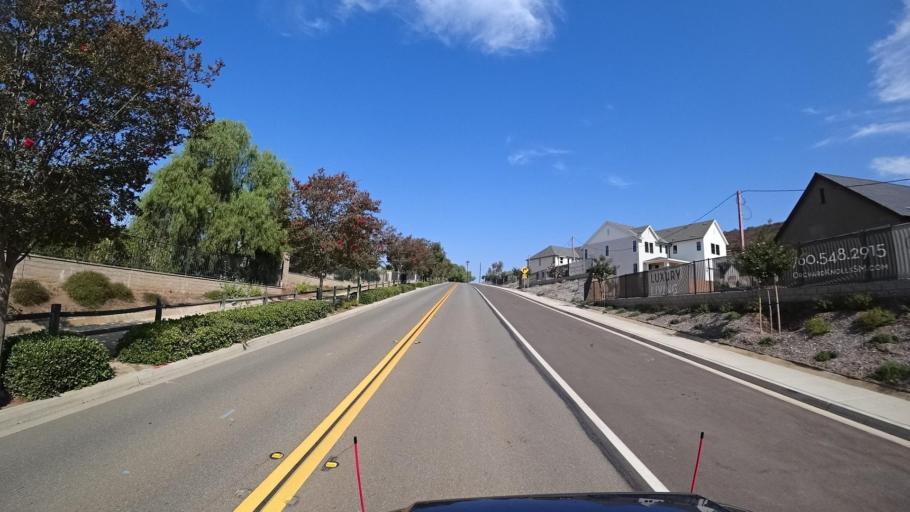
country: US
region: California
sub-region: San Diego County
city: San Marcos
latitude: 33.1631
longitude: -117.1446
